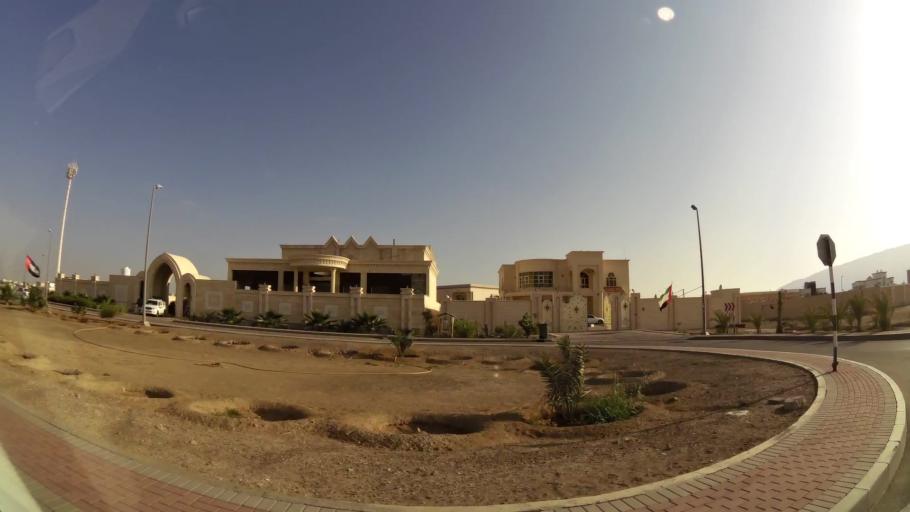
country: AE
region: Abu Dhabi
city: Al Ain
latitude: 24.0726
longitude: 55.8520
